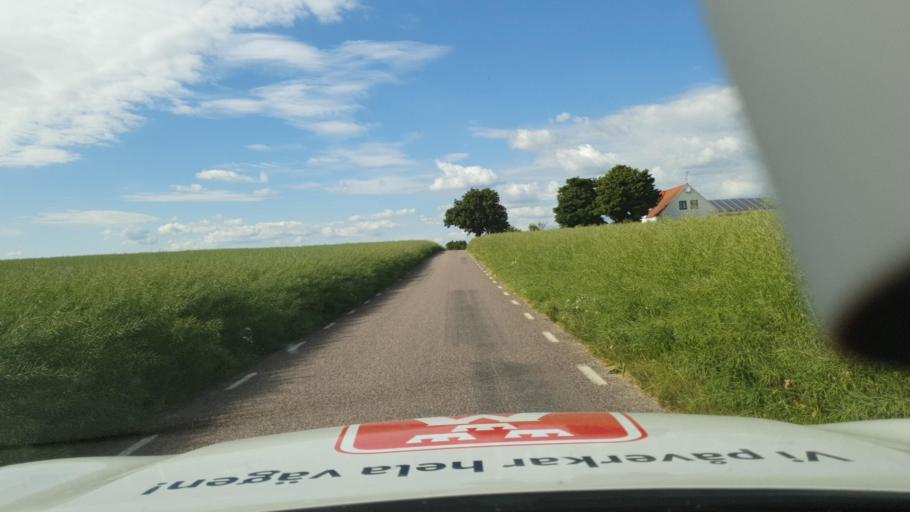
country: SE
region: Skane
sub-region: Skurups Kommun
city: Skurup
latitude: 55.4487
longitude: 13.5186
